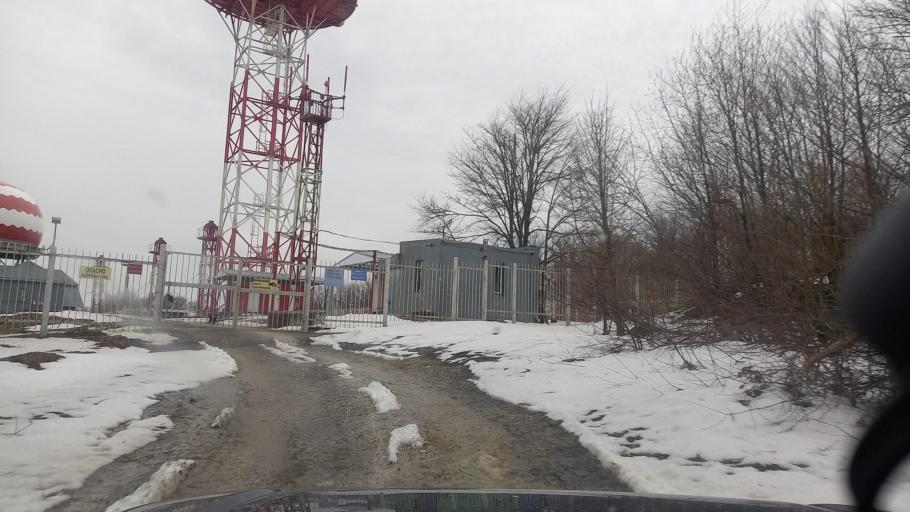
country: RU
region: Krasnodarskiy
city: Pshada
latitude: 44.5971
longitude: 38.3245
